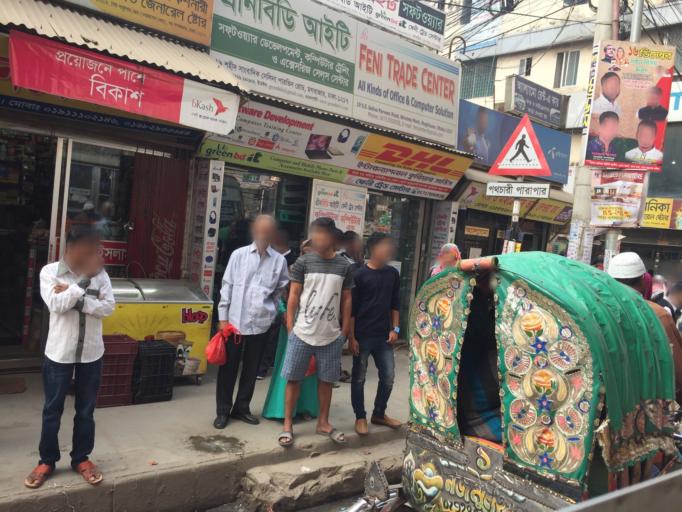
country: BD
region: Dhaka
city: Paltan
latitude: 23.7482
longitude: 90.4086
